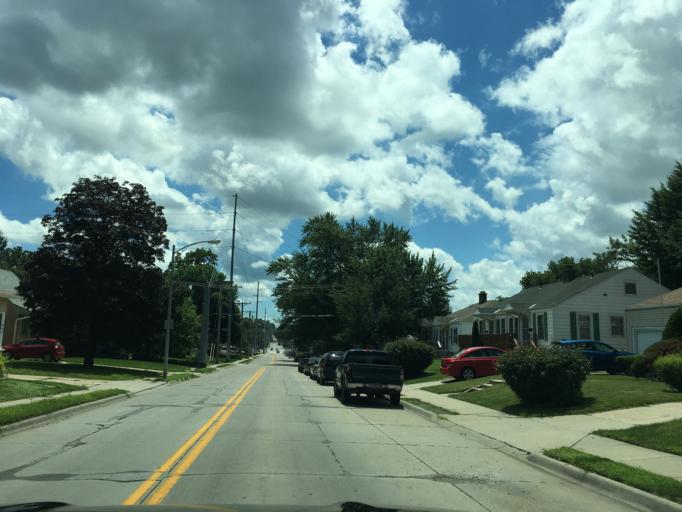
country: US
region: Nebraska
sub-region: Douglas County
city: Omaha
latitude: 41.2496
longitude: -95.9902
